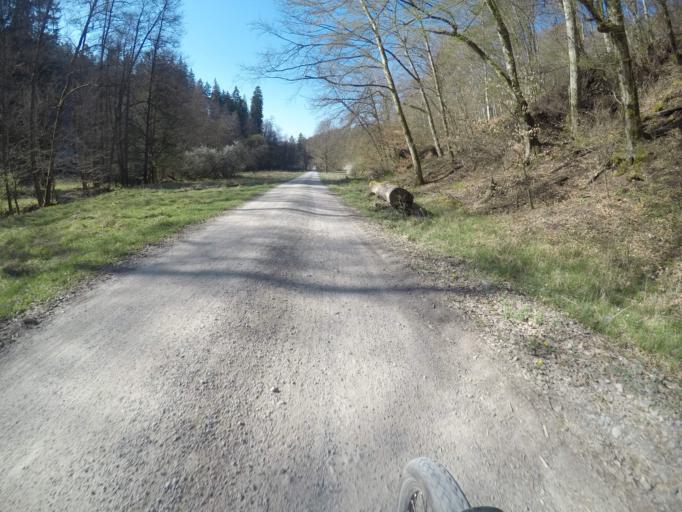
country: DE
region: Baden-Wuerttemberg
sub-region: Regierungsbezirk Stuttgart
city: Weil im Schonbuch
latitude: 48.5792
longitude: 9.0358
